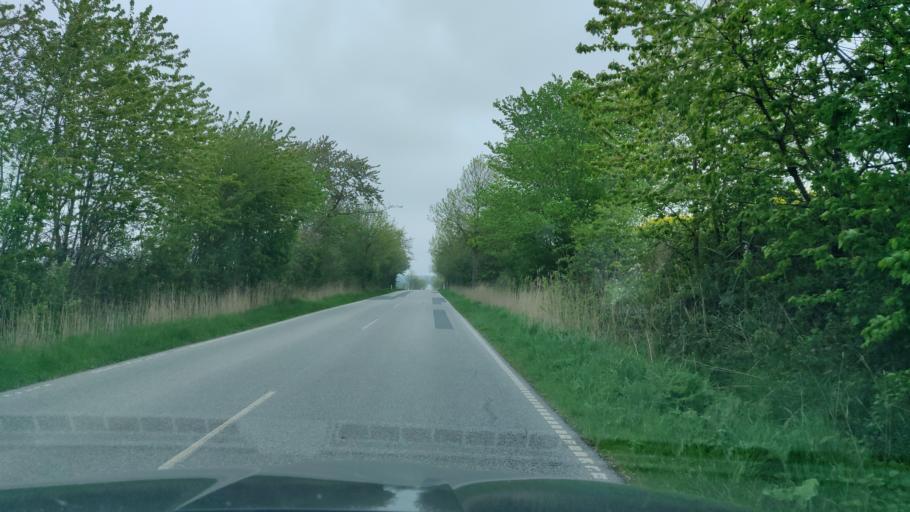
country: DK
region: South Denmark
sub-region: Sonderborg Kommune
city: Guderup
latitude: 54.9939
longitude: 9.8974
